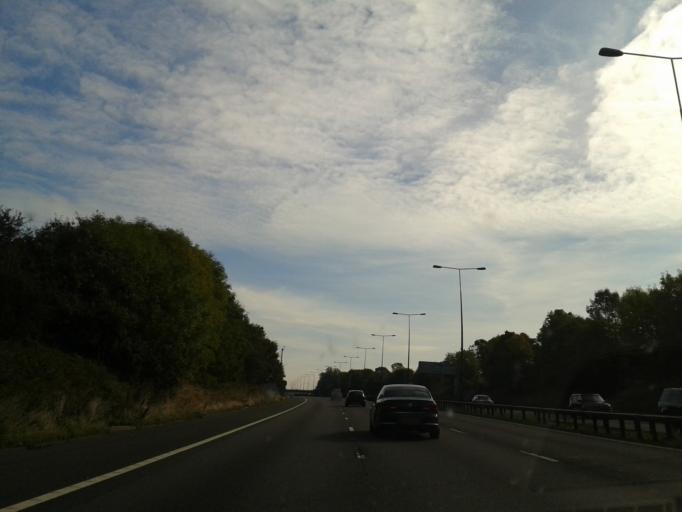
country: GB
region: England
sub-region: Staffordshire
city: Audley
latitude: 52.9940
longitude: -2.3023
